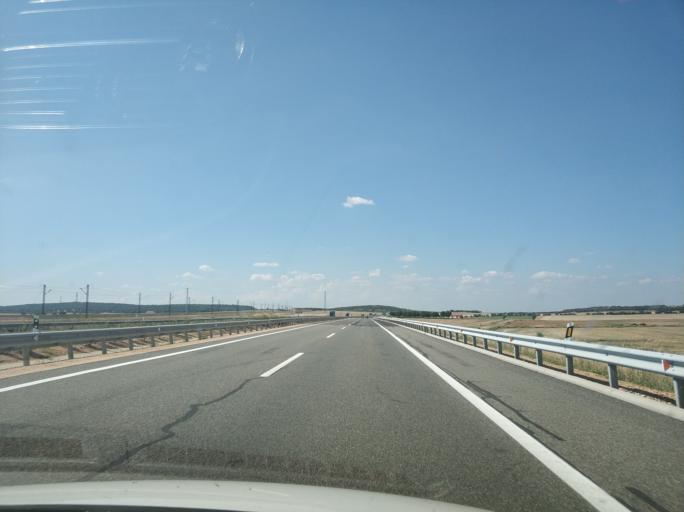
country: ES
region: Castille and Leon
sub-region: Provincia de Zamora
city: Montamarta
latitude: 41.6682
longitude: -5.8008
